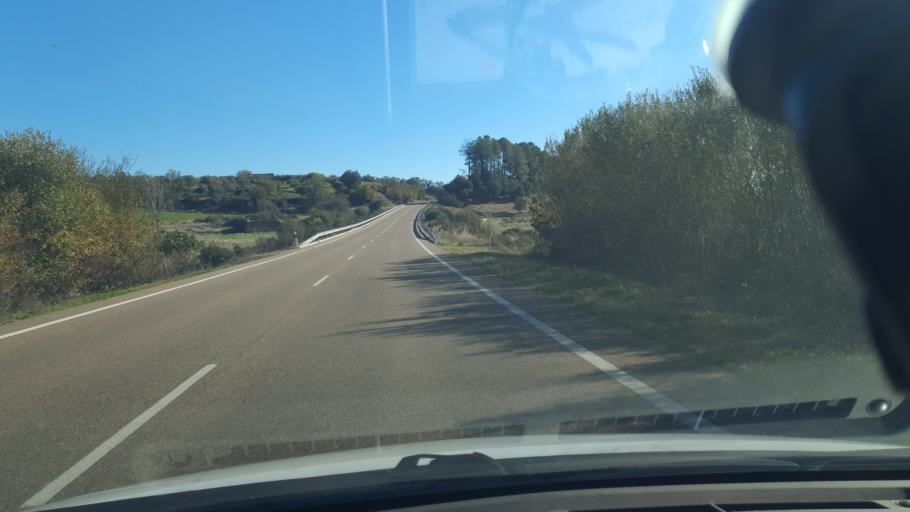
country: ES
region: Castille and Leon
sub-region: Provincia de Avila
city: Candeleda
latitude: 40.1371
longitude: -5.2408
